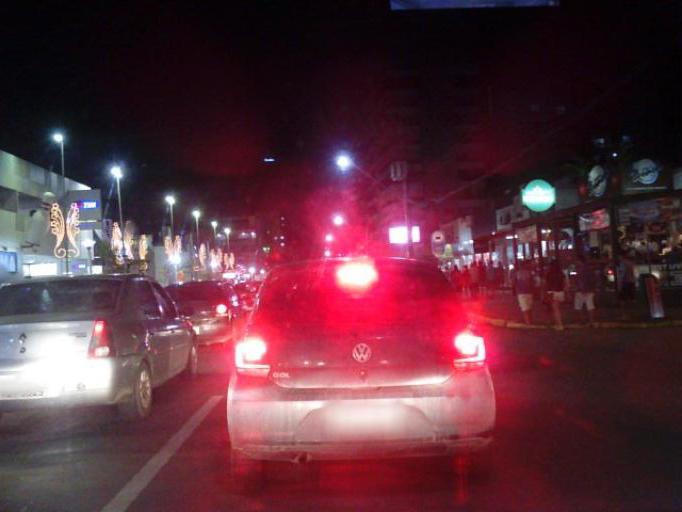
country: BR
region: Santa Catarina
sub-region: Itapema
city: Itapema
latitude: -27.1271
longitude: -48.6026
